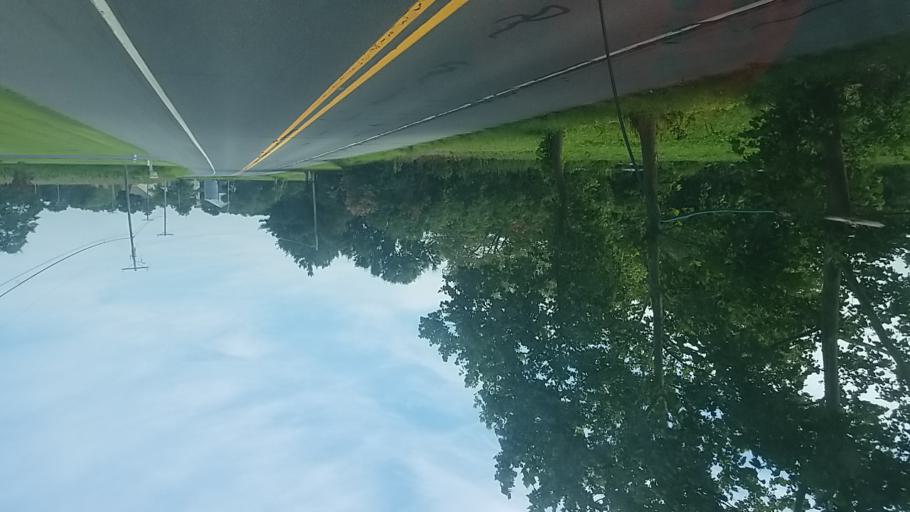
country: US
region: Delaware
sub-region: Sussex County
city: Selbyville
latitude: 38.5318
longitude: -75.1917
